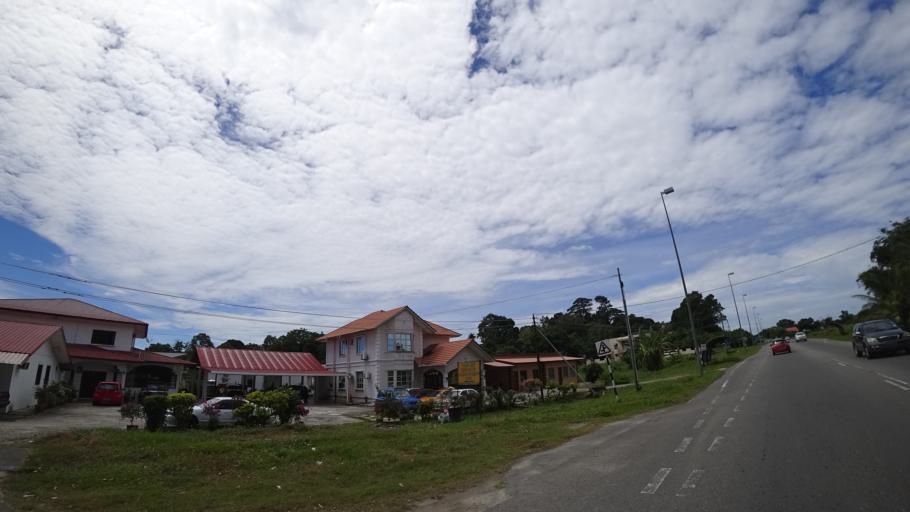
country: MY
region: Sarawak
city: Limbang
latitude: 4.8018
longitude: 114.8312
